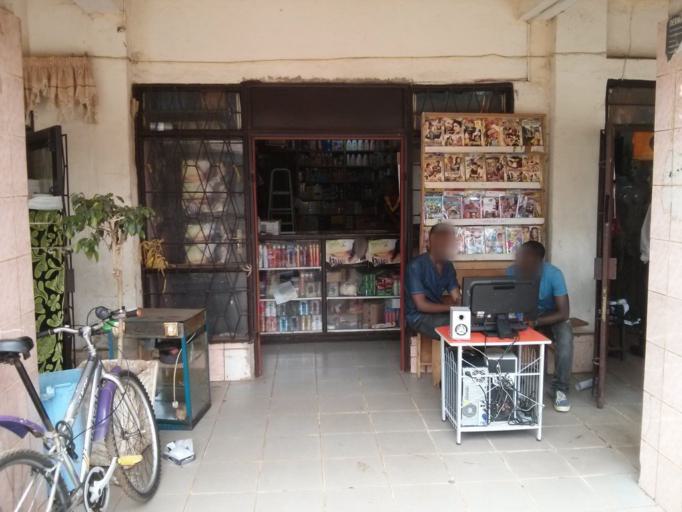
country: RW
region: Kigali
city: Kigali
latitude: -1.9448
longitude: 30.0585
